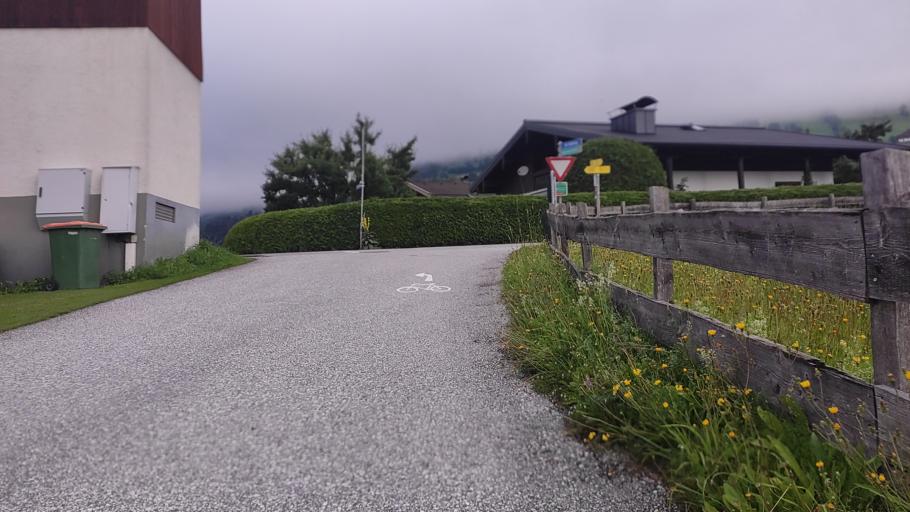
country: AT
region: Salzburg
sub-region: Politischer Bezirk Zell am See
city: Niedernsill
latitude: 47.2817
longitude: 12.6228
